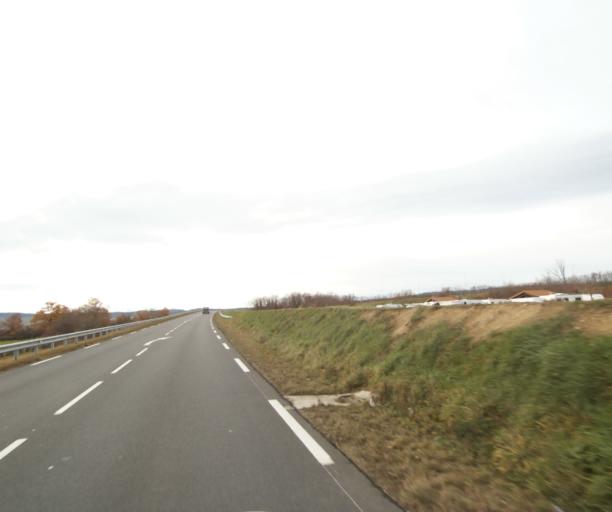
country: FR
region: Rhone-Alpes
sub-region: Departement de la Loire
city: Sury-le-Comtal
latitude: 45.5266
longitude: 4.1961
